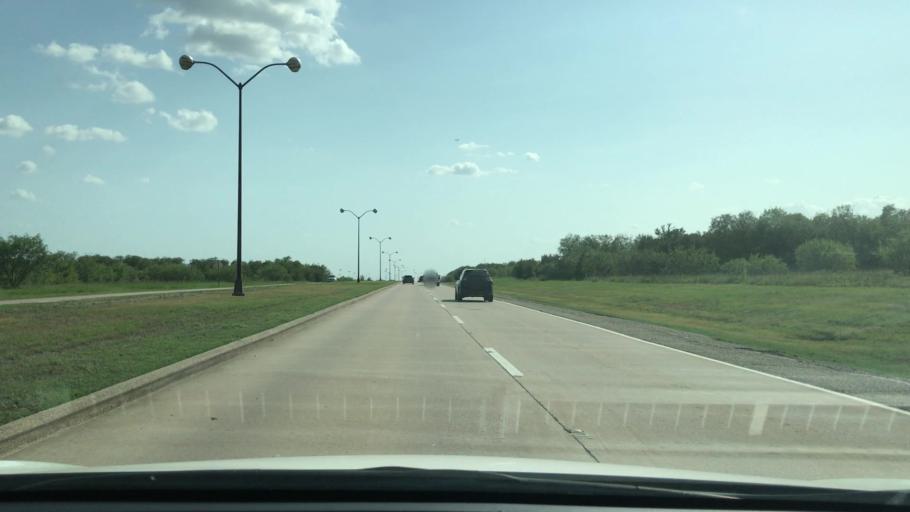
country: US
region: Texas
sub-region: Tarrant County
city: Euless
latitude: 32.8671
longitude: -97.0201
